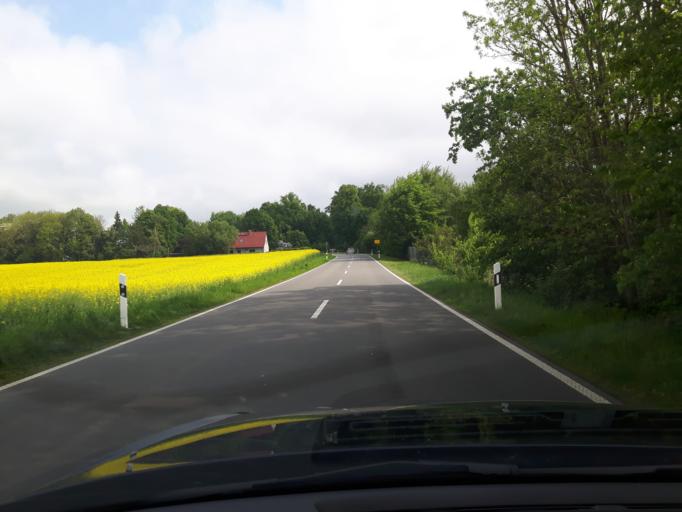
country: DE
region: Mecklenburg-Vorpommern
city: Gross Wokern
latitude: 53.6389
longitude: 12.4833
